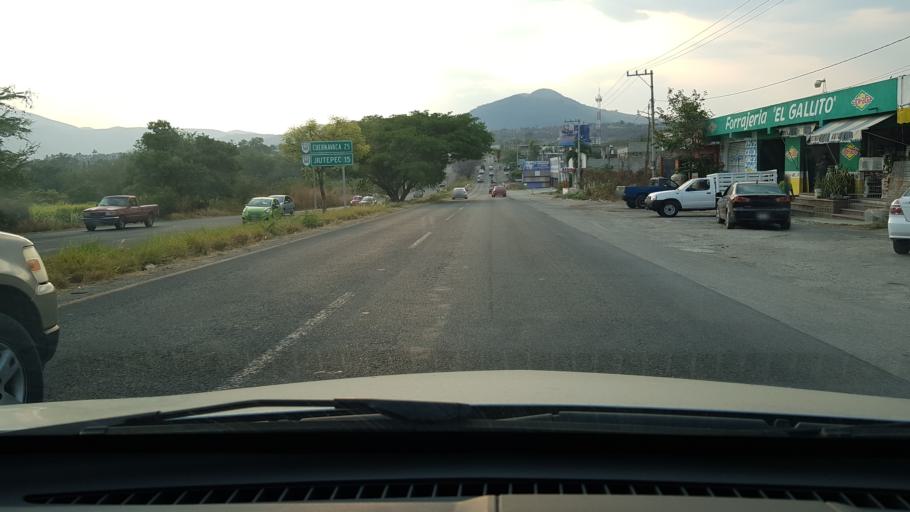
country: MX
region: Morelos
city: Yautepec
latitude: 18.8708
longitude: -99.0692
